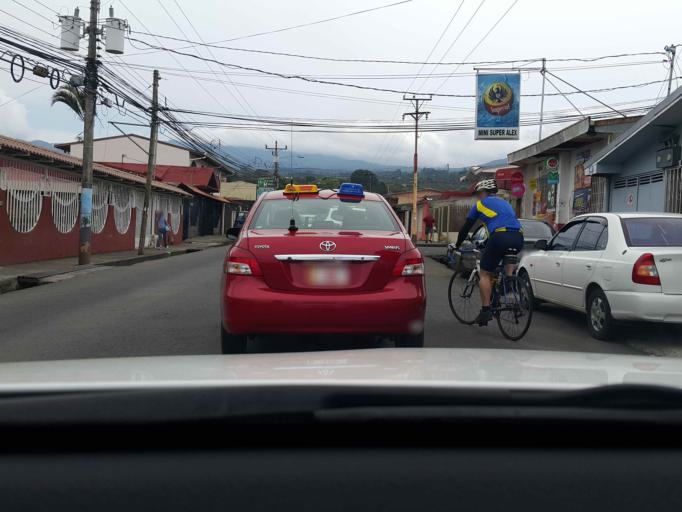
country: CR
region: Heredia
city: San Rafael
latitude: 10.0134
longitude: -84.0967
